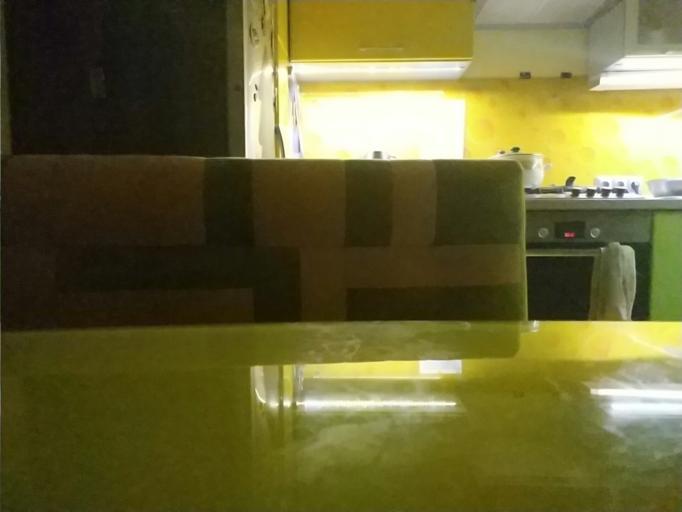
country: RU
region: Republic of Karelia
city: Pyaozerskiy
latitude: 65.5212
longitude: 30.6004
